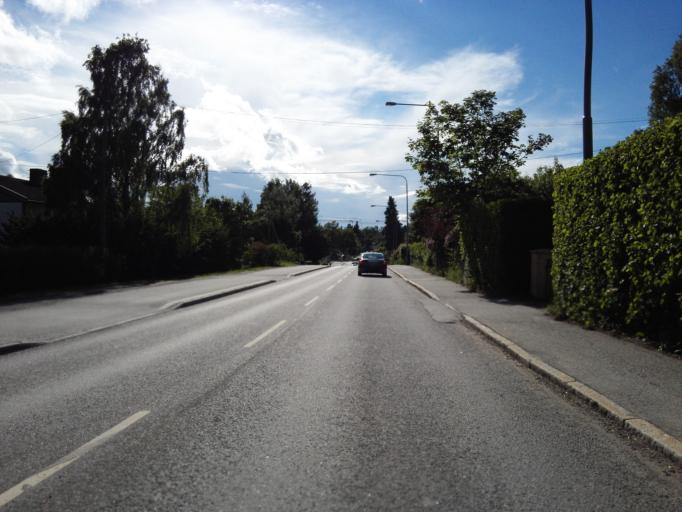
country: SE
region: Stockholm
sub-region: Huddinge Kommun
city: Huddinge
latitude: 59.2419
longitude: 18.0092
